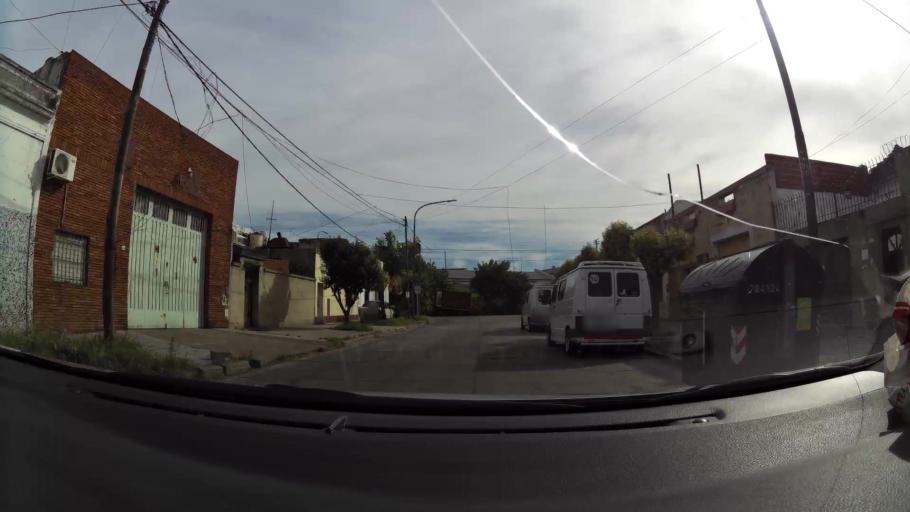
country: AR
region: Buenos Aires F.D.
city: Buenos Aires
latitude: -34.6466
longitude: -58.4228
